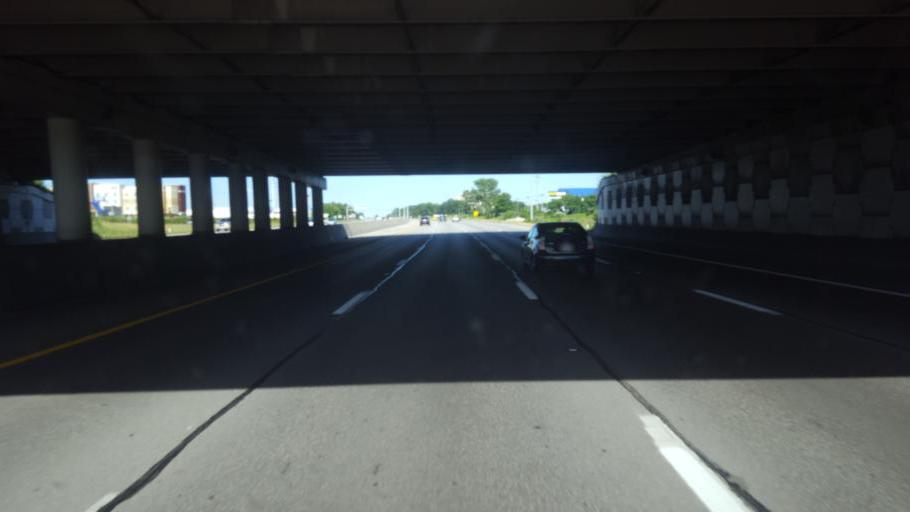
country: US
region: Ohio
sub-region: Franklin County
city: Dublin
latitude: 40.1089
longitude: -83.0914
